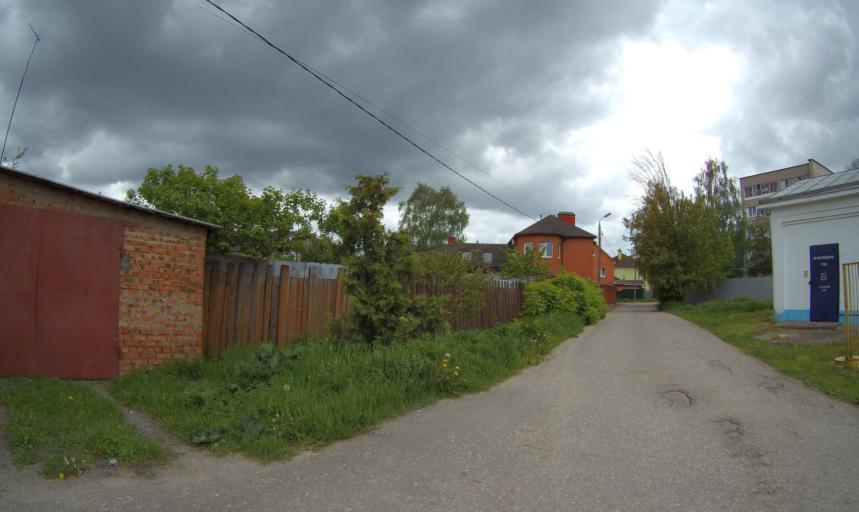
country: RU
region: Moskovskaya
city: Kolomna
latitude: 55.1016
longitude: 38.7799
